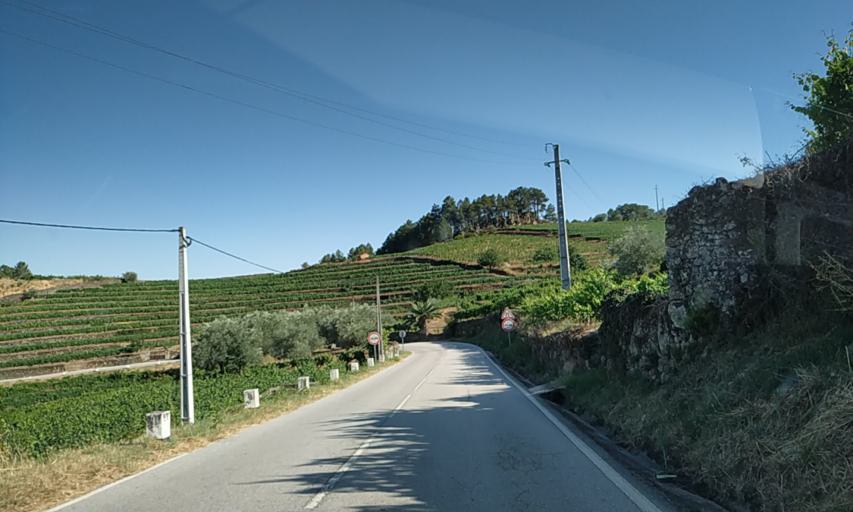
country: PT
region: Viseu
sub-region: Sao Joao da Pesqueira
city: Sao Joao da Pesqueira
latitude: 41.2542
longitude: -7.4408
